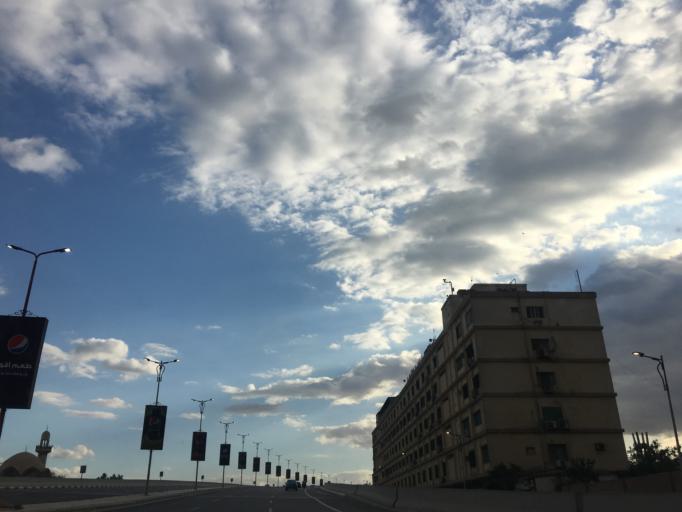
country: EG
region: Muhafazat al Qahirah
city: Cairo
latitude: 30.0454
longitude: 31.3079
